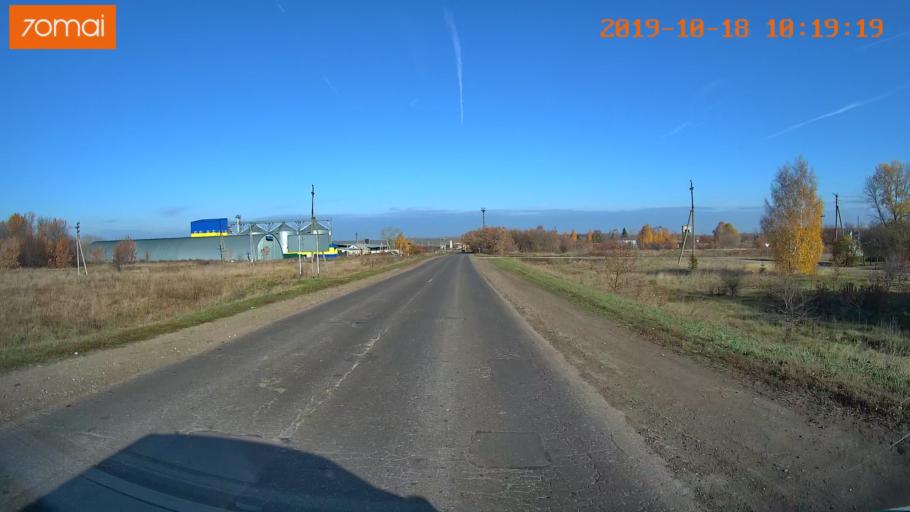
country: RU
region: Tula
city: Kurkino
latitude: 53.4209
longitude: 38.6456
